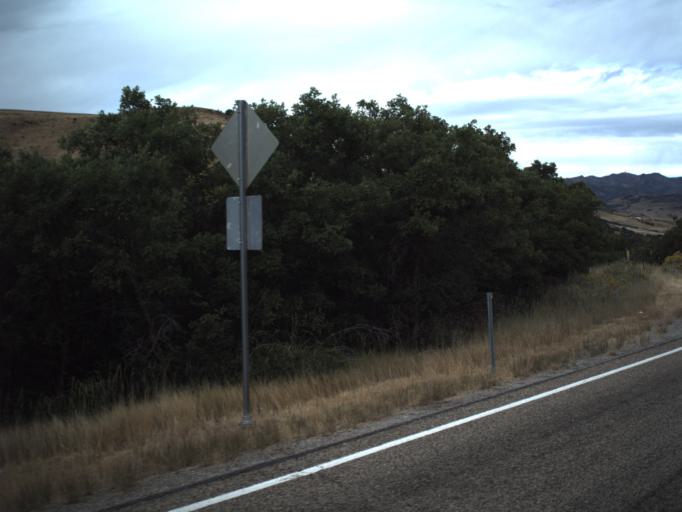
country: US
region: Utah
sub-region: Morgan County
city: Morgan
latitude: 40.9392
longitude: -111.6418
